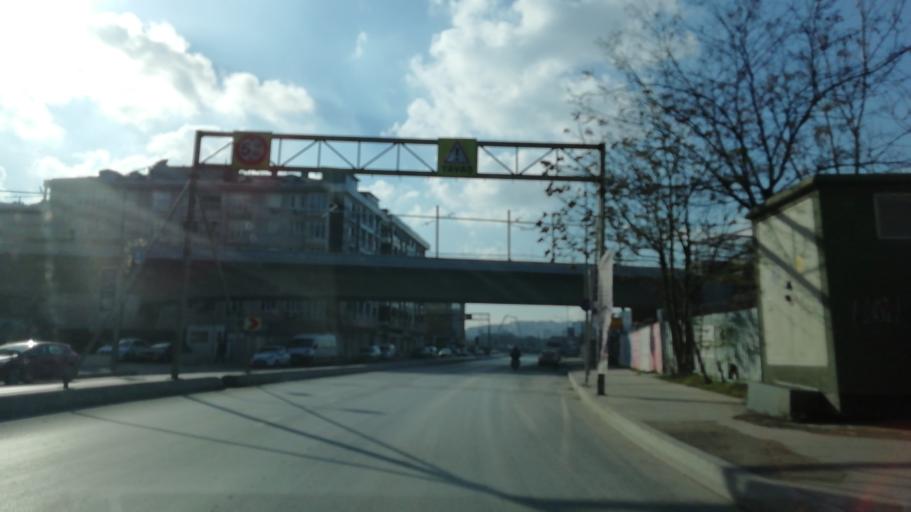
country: TR
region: Istanbul
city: Sisli
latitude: 41.0795
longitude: 28.9513
